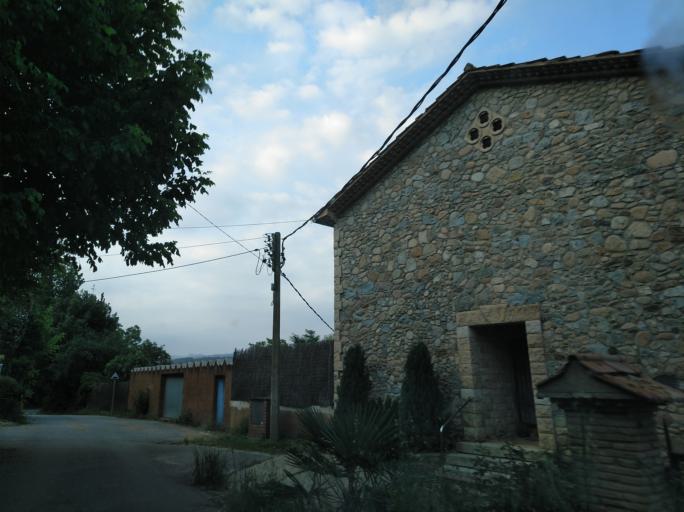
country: ES
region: Catalonia
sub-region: Provincia de Girona
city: la Cellera de Ter
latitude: 41.9570
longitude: 2.6217
